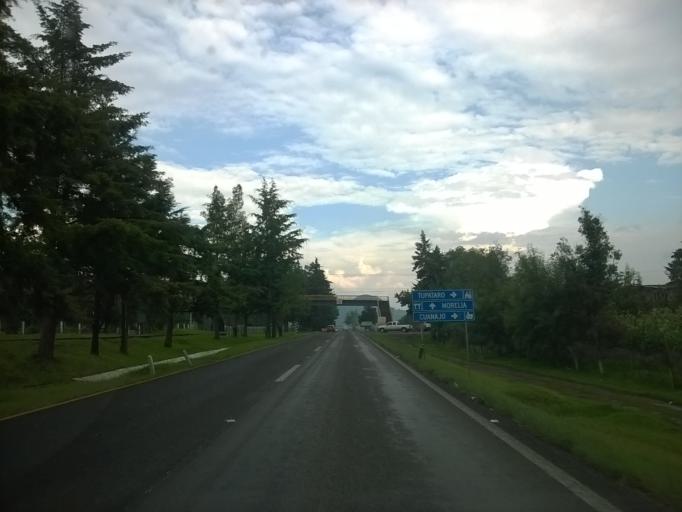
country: MX
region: Michoacan
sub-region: Huiramba
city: El Pedregal
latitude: 19.5308
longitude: -101.4844
